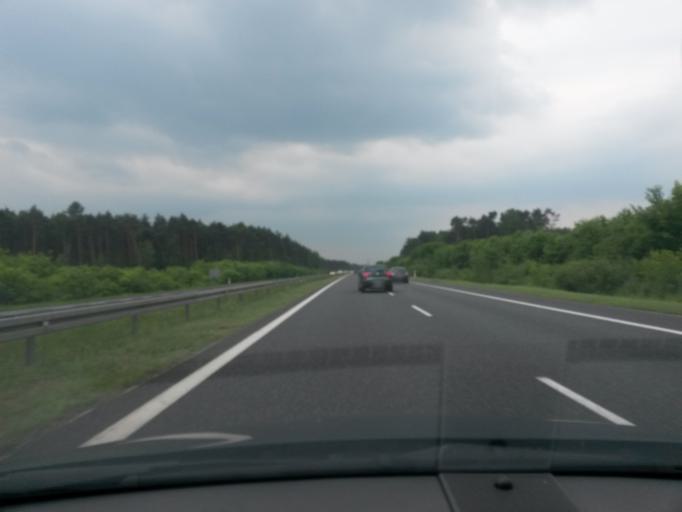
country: PL
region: Lodz Voivodeship
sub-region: Powiat radomszczanski
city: Radomsko
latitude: 51.0438
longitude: 19.3470
